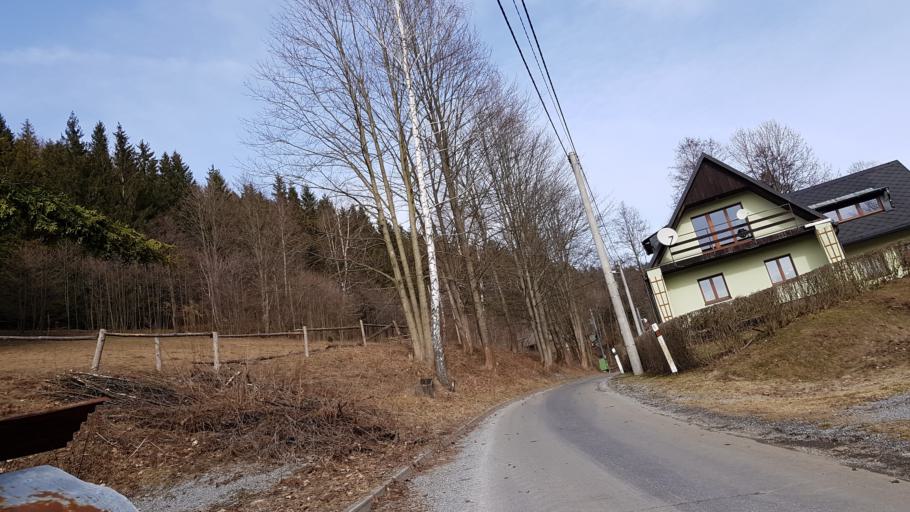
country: CZ
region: Olomoucky
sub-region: Okres Jesenik
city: Jesenik
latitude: 50.2239
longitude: 17.2272
